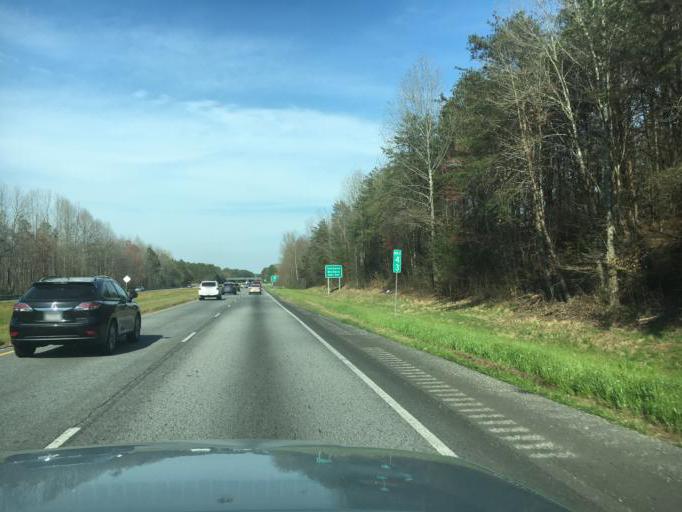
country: US
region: Georgia
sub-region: Habersham County
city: Baldwin
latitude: 34.5099
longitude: -83.5623
